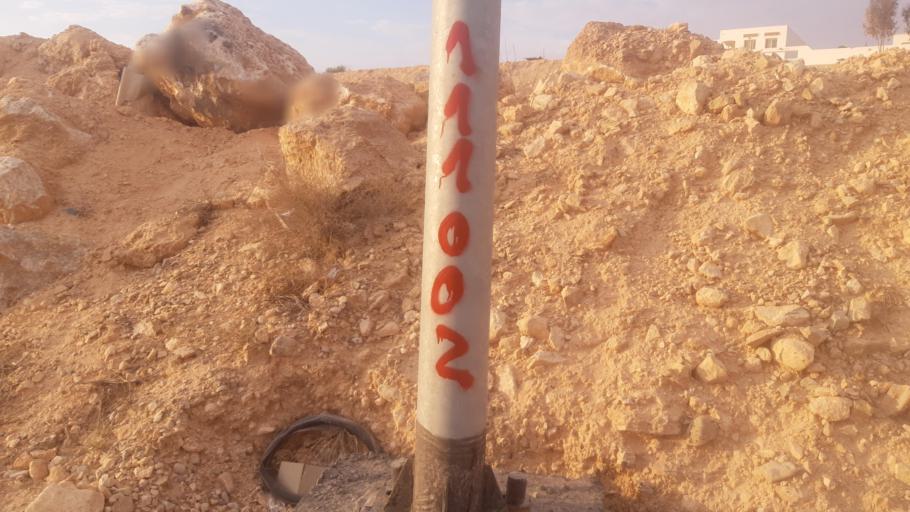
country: TN
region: Tataouine
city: Tataouine
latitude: 32.9964
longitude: 10.5041
